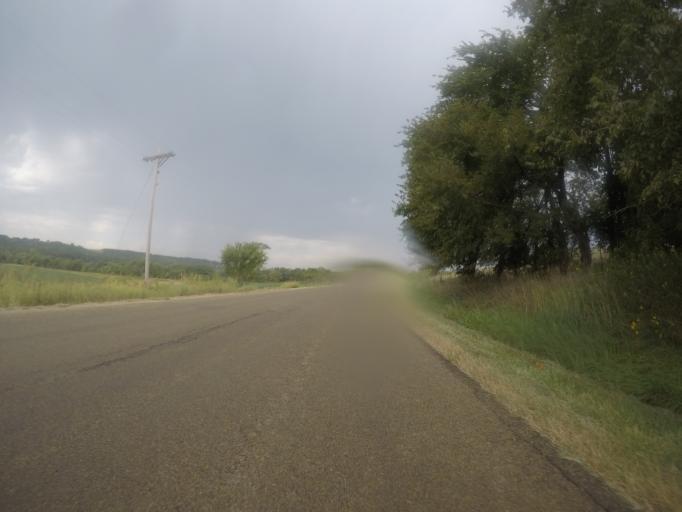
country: US
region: Kansas
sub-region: Riley County
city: Ogden
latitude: 39.0367
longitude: -96.7125
